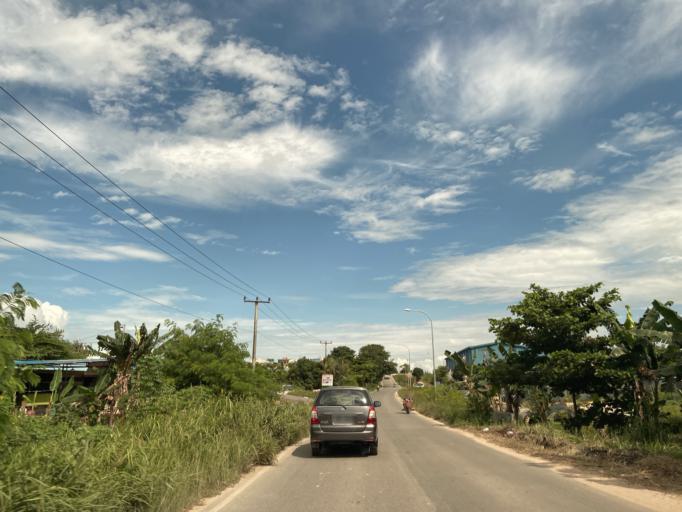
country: SG
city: Singapore
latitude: 1.0291
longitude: 103.9437
